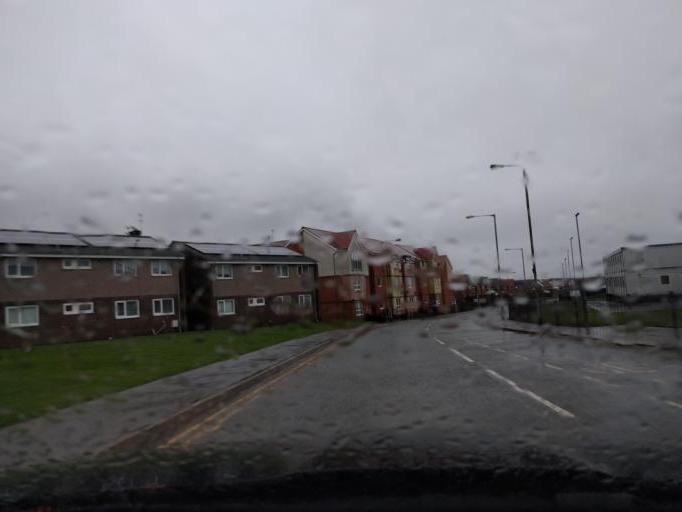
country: GB
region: England
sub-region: Northumberland
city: Lynemouth
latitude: 55.1848
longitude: -1.5484
